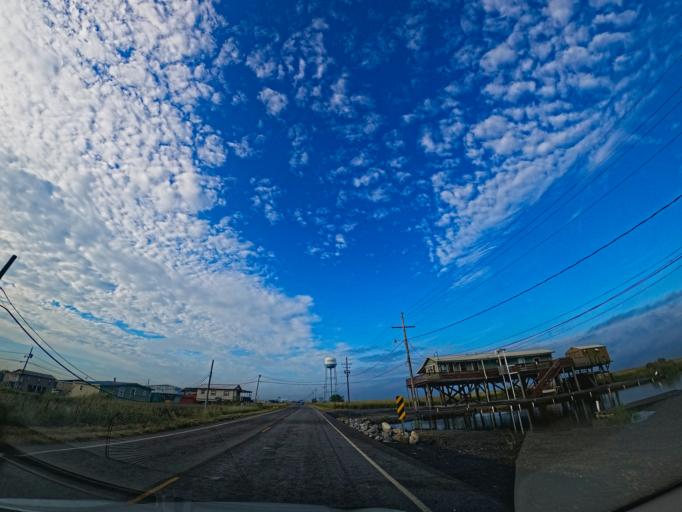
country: US
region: Louisiana
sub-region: Terrebonne Parish
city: Dulac
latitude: 29.2691
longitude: -90.6498
